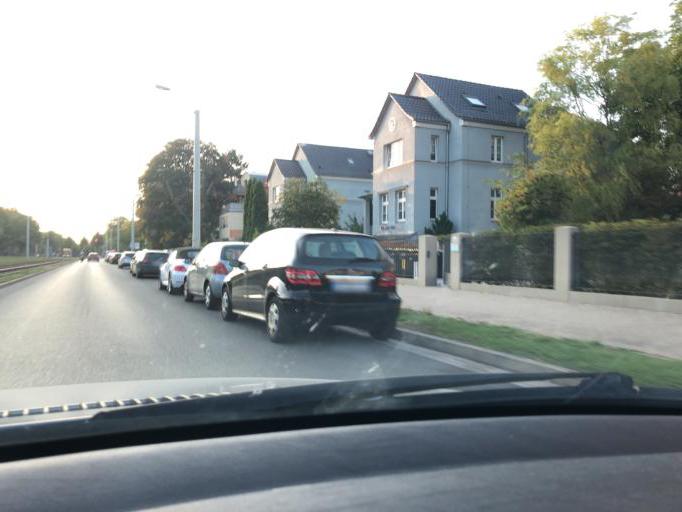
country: DE
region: Saxony
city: Dresden
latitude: 51.0359
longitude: 13.7812
